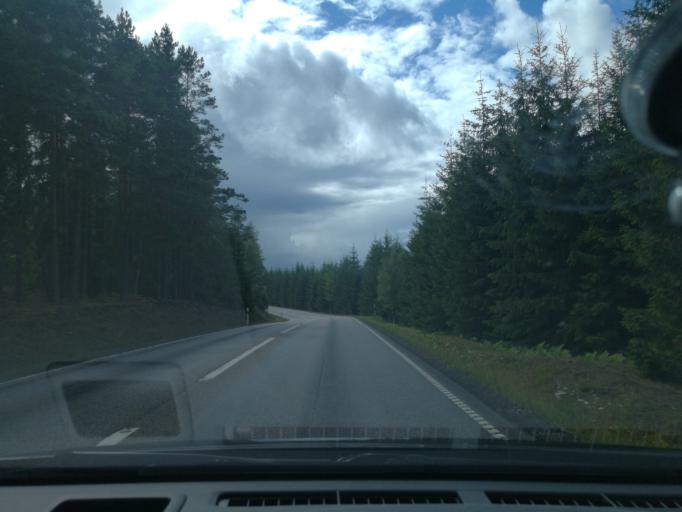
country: SE
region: OErebro
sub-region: Hallsbergs Kommun
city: Palsboda
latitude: 58.8787
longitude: 15.4190
